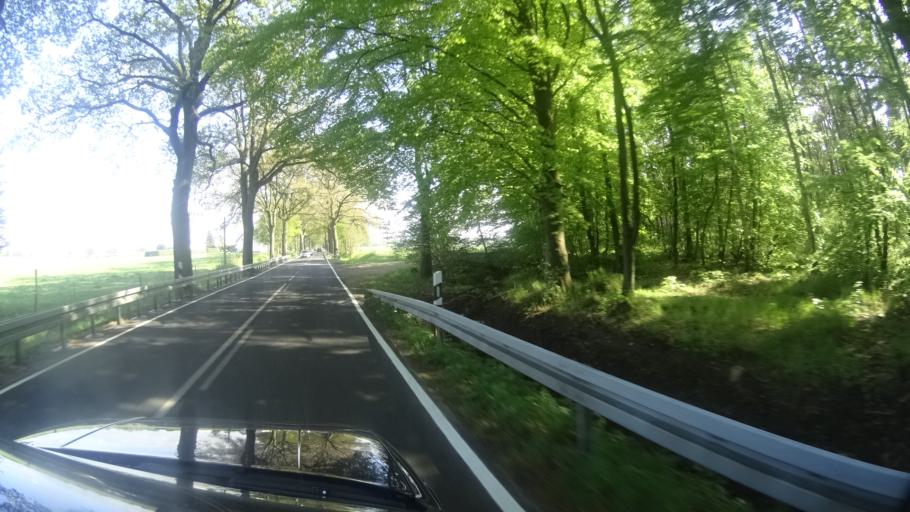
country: DE
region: Mecklenburg-Vorpommern
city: Gelbensande
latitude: 54.2502
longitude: 12.3116
